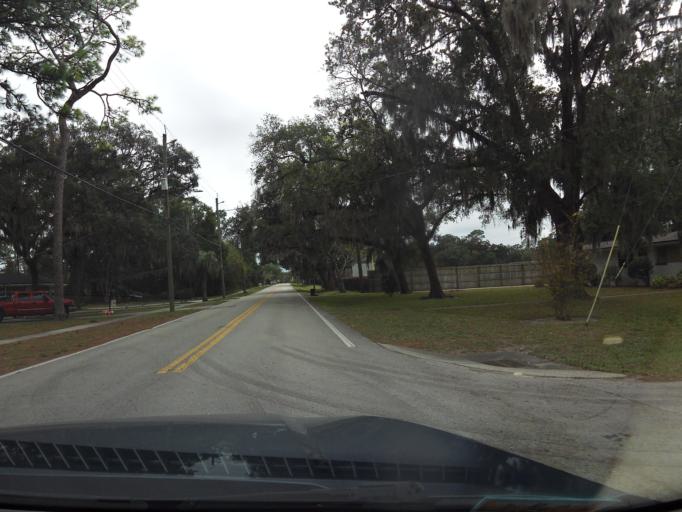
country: US
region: Florida
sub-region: Duval County
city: Jacksonville
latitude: 30.3049
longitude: -81.6030
